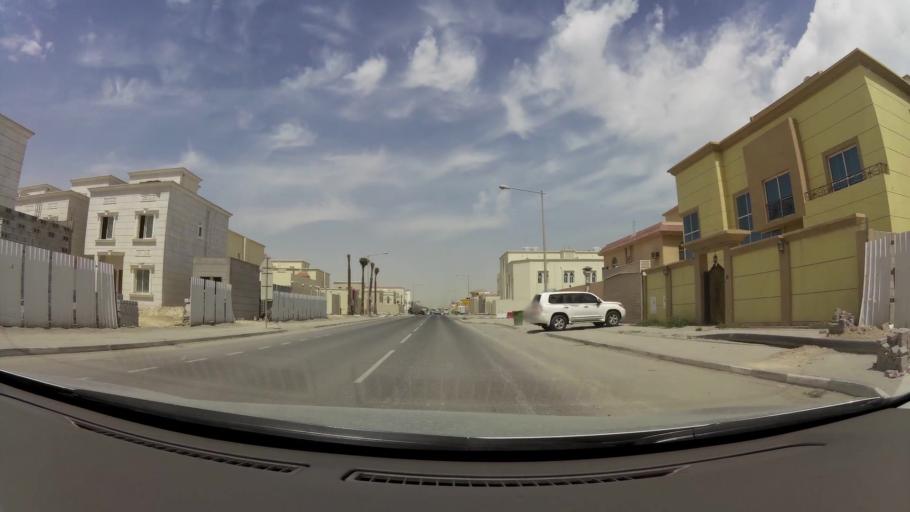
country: QA
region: Baladiyat ar Rayyan
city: Ar Rayyan
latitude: 25.2631
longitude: 51.4263
